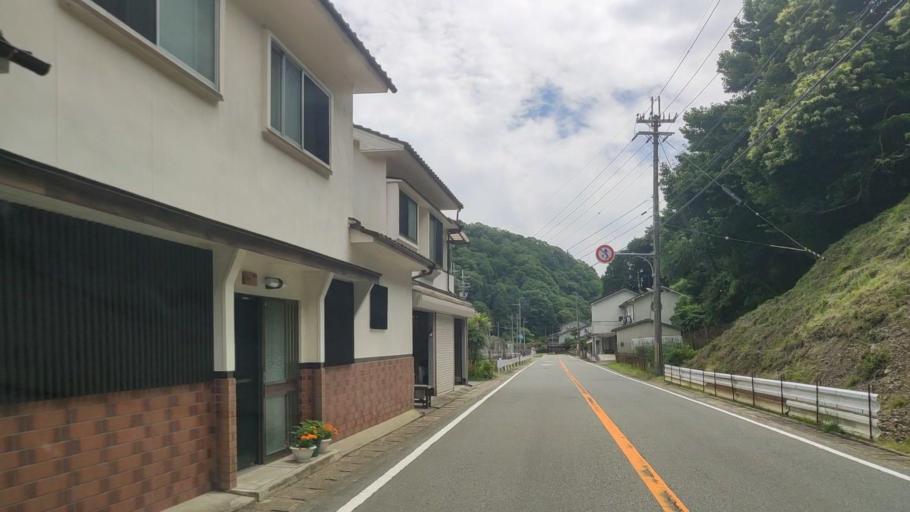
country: JP
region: Hyogo
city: Yamazakicho-nakabirose
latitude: 35.1007
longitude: 134.3629
